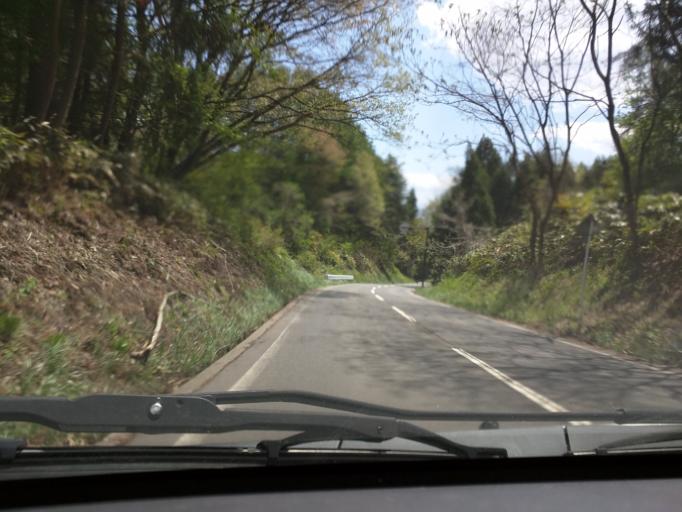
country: JP
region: Nagano
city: Nagano-shi
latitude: 36.6935
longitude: 138.1524
